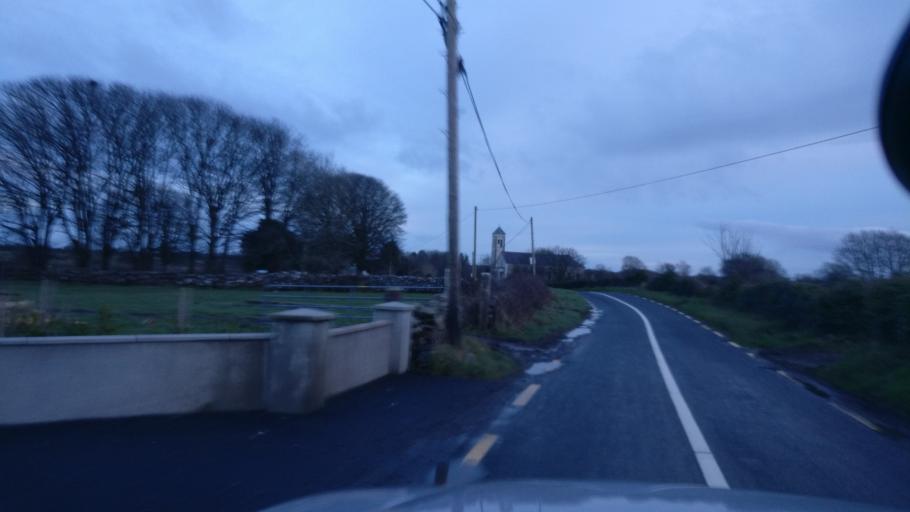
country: IE
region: Connaught
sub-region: County Galway
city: Athenry
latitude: 53.2529
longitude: -8.6745
